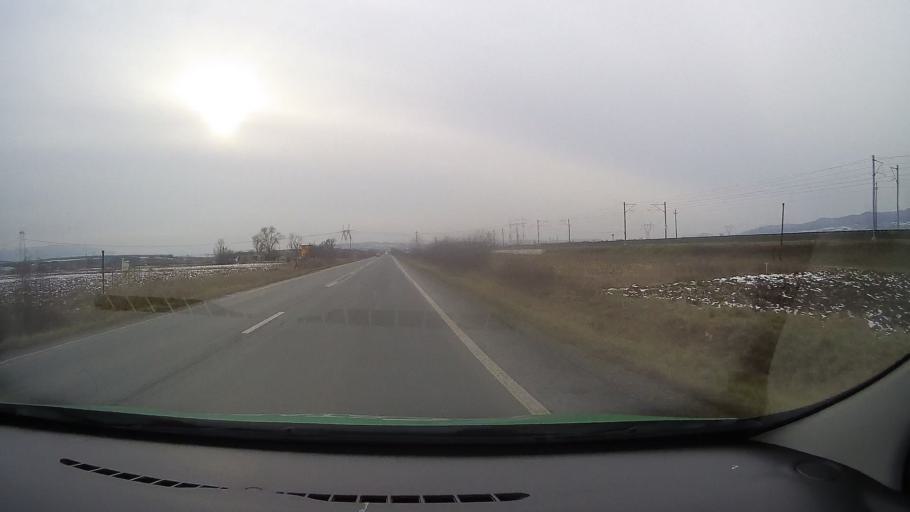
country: RO
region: Hunedoara
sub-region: Comuna Geoagiu
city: Geoagiu
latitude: 45.8775
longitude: 23.2400
